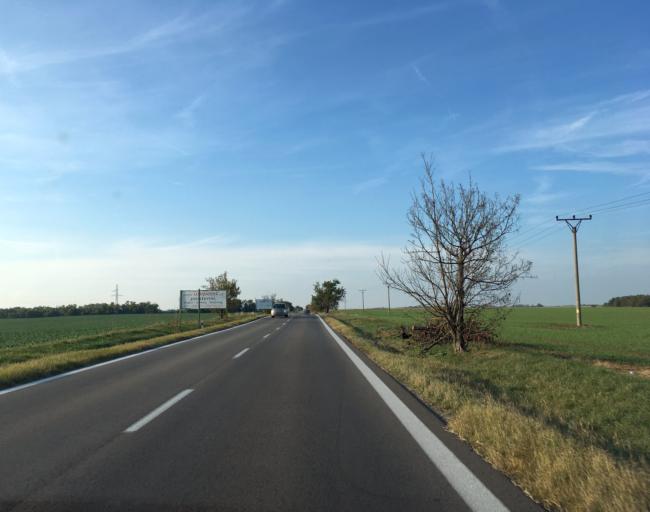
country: SK
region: Nitriansky
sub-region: Okres Nove Zamky
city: Nove Zamky
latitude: 48.0214
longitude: 18.1440
